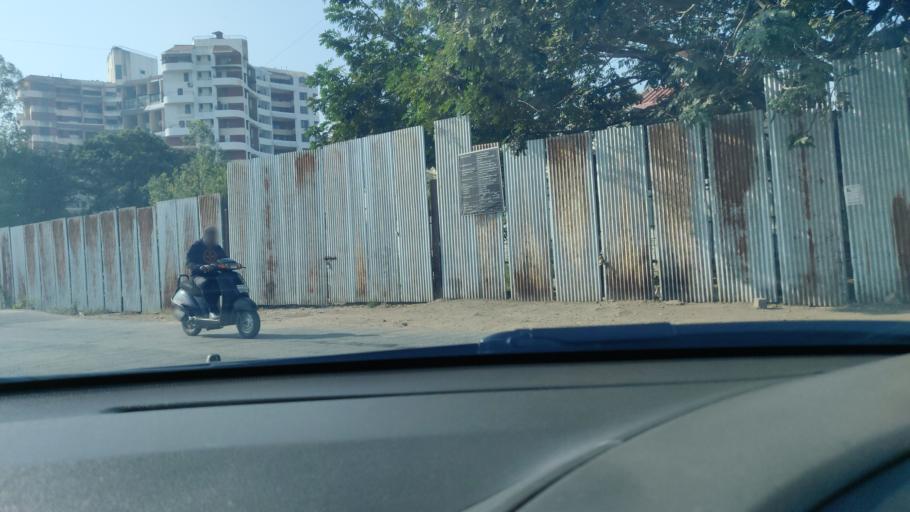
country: IN
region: Maharashtra
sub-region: Pune Division
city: Khadki
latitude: 18.5615
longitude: 73.7922
